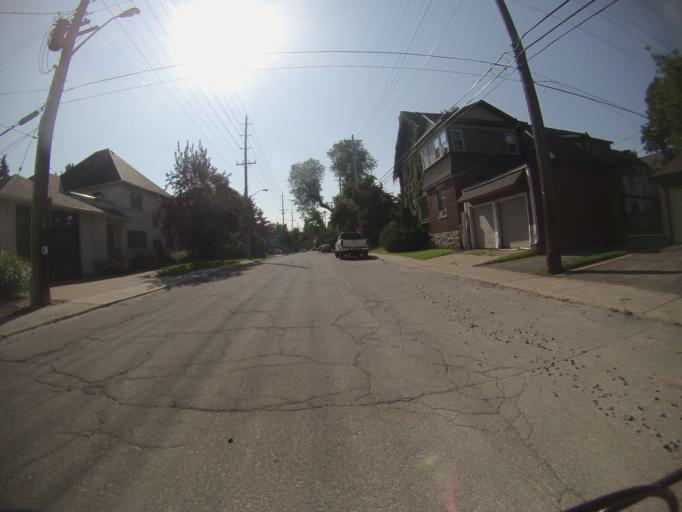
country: CA
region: Ontario
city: Ottawa
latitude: 45.4057
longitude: -75.6940
